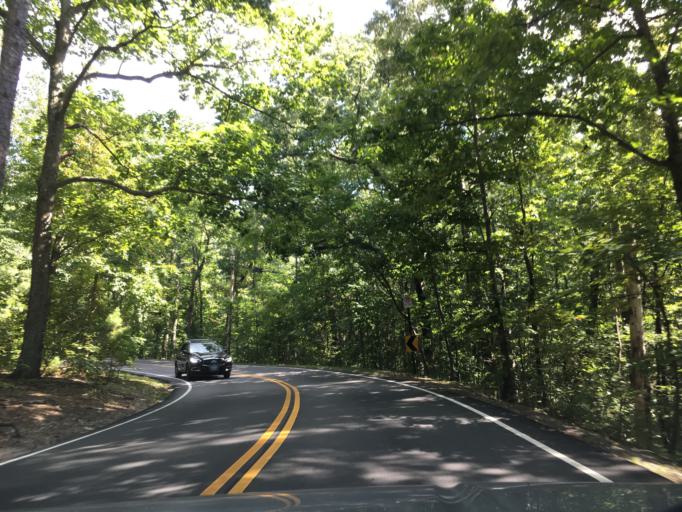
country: US
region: Virginia
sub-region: Henrico County
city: Tuckahoe
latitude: 37.5822
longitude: -77.5338
